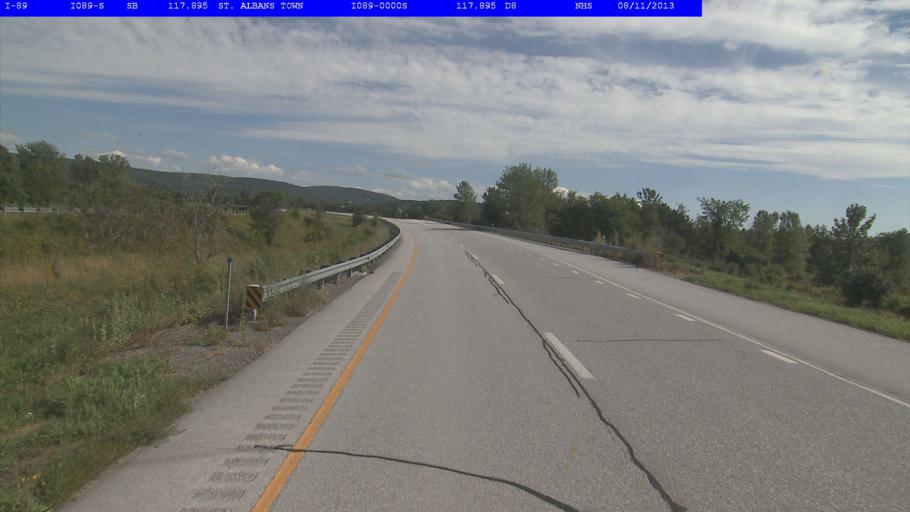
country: US
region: Vermont
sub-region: Franklin County
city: Saint Albans
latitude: 44.8467
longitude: -73.0829
